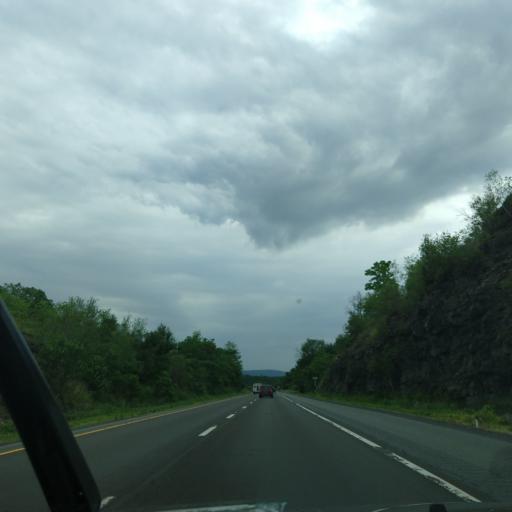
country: US
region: Pennsylvania
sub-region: Luzerne County
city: Laflin
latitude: 41.2836
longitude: -75.7889
